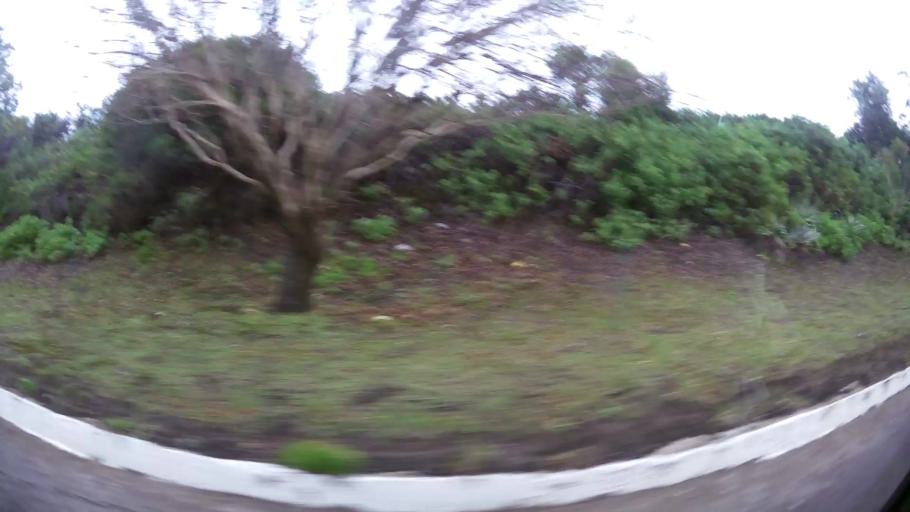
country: ZA
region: Eastern Cape
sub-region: Nelson Mandela Bay Metropolitan Municipality
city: Port Elizabeth
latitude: -33.9354
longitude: 25.5458
